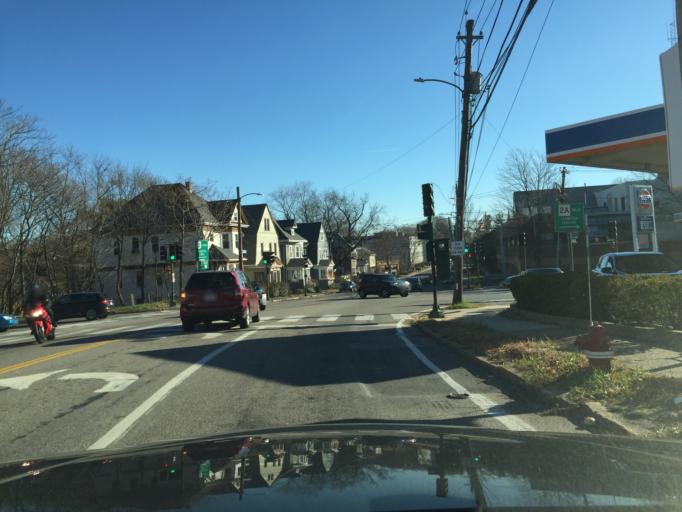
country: US
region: Massachusetts
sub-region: Middlesex County
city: Arlington
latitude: 42.4200
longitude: -71.1526
